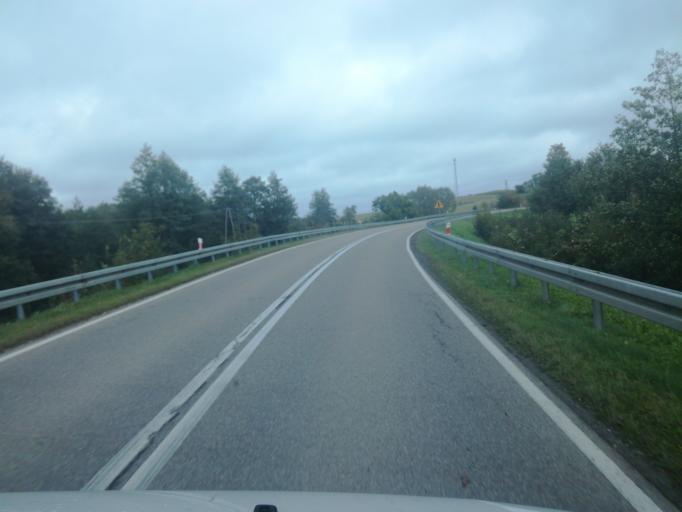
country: PL
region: Podlasie
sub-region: Powiat sejnenski
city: Sejny
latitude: 54.1141
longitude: 23.4240
